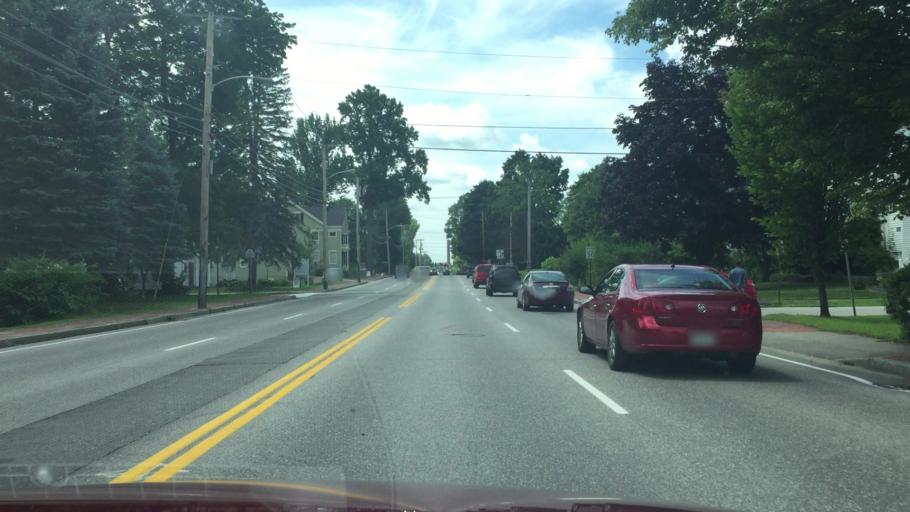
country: US
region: Maine
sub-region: York County
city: Saco
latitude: 43.5040
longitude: -70.4399
